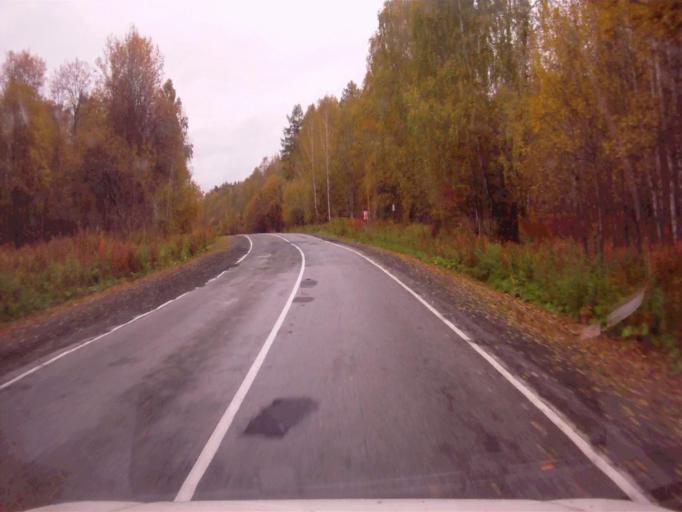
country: RU
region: Chelyabinsk
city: Nizhniy Ufaley
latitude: 56.0520
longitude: 59.9504
